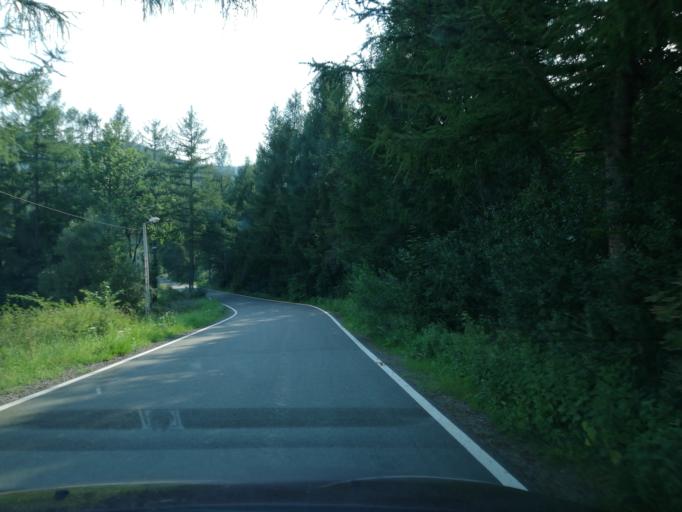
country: PL
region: Lesser Poland Voivodeship
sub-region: Powiat nowosadecki
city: Nawojowa
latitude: 49.5341
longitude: 20.7414
